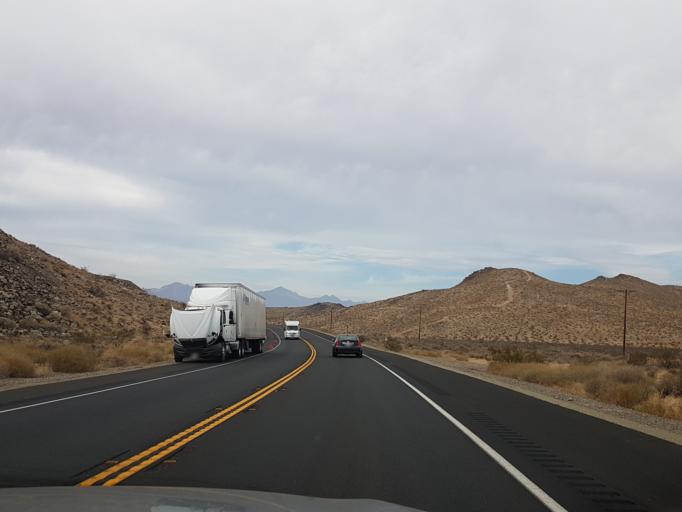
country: US
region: California
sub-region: Kern County
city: Ridgecrest
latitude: 35.5430
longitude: -117.6894
